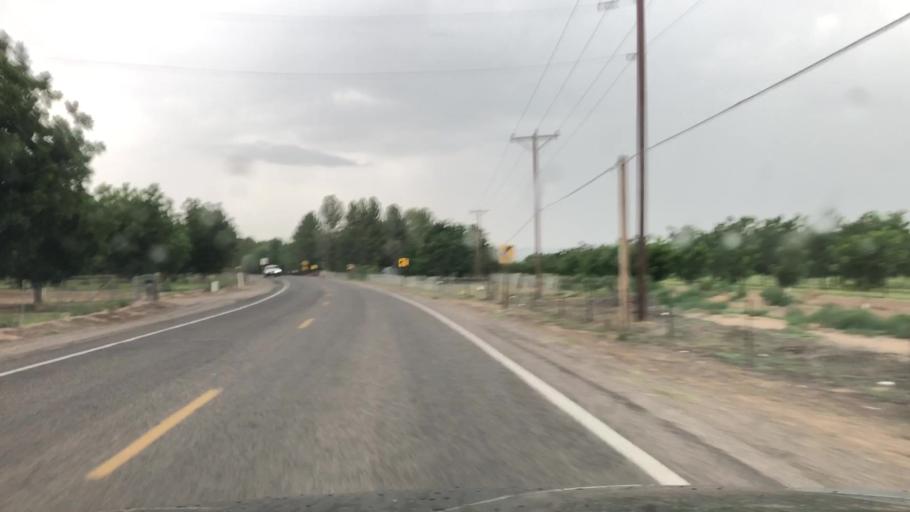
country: US
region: New Mexico
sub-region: Dona Ana County
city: Vado
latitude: 32.1116
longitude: -106.6741
